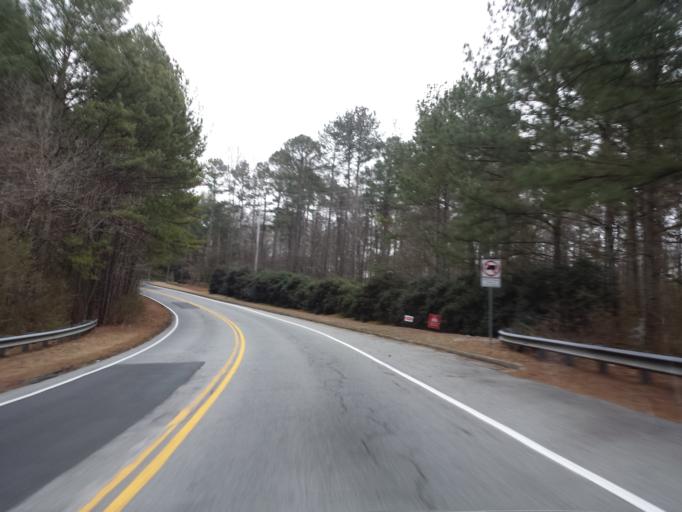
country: US
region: Georgia
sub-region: Fulton County
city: Roswell
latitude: 34.0145
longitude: -84.3998
